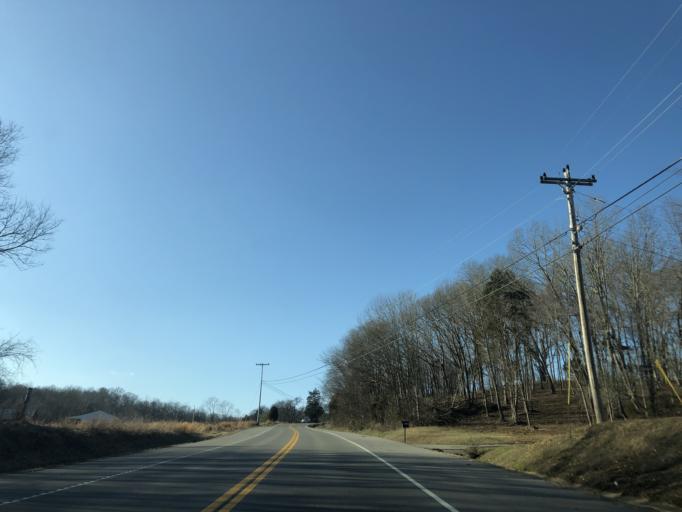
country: US
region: Tennessee
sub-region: Sumner County
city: White House
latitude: 36.4675
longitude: -86.5628
